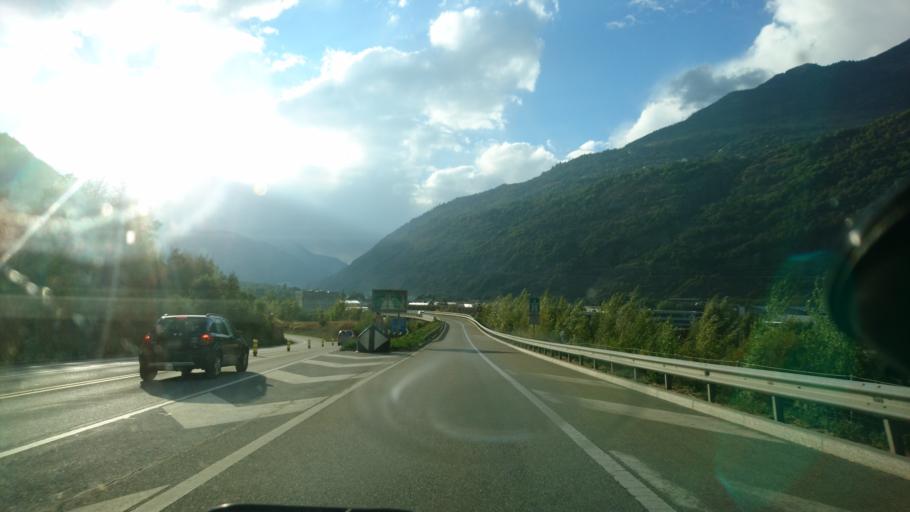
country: CH
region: Valais
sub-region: Brig District
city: Brig
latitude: 46.3060
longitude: 7.9682
